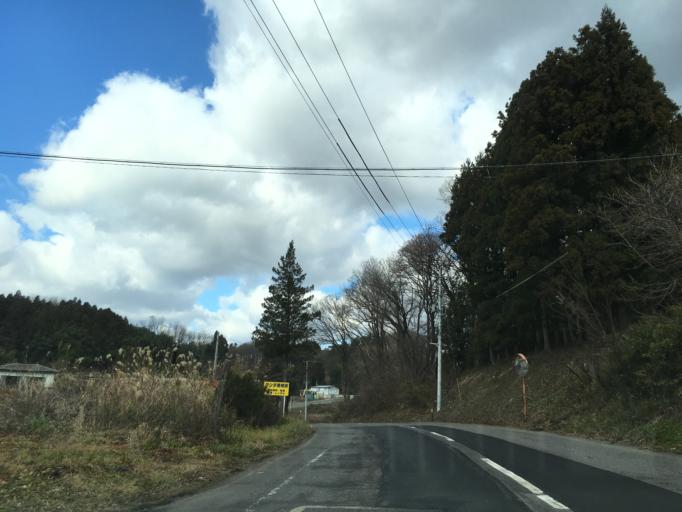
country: JP
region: Fukushima
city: Sukagawa
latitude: 37.3292
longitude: 140.4405
